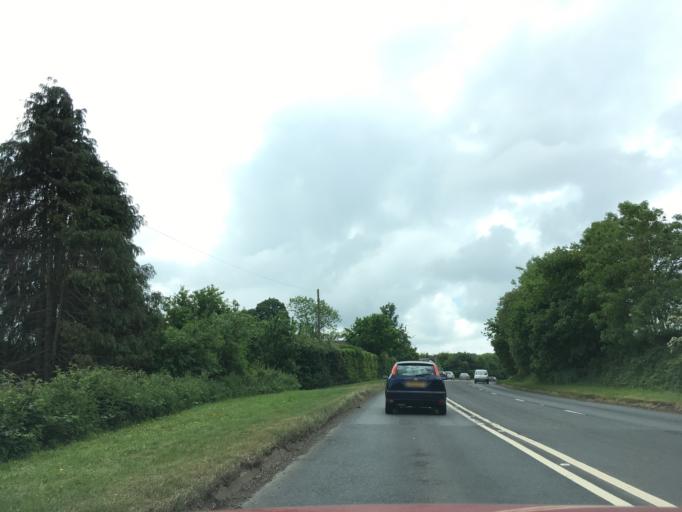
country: GB
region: England
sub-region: Devon
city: Uffculme
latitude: 50.9242
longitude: -3.3249
